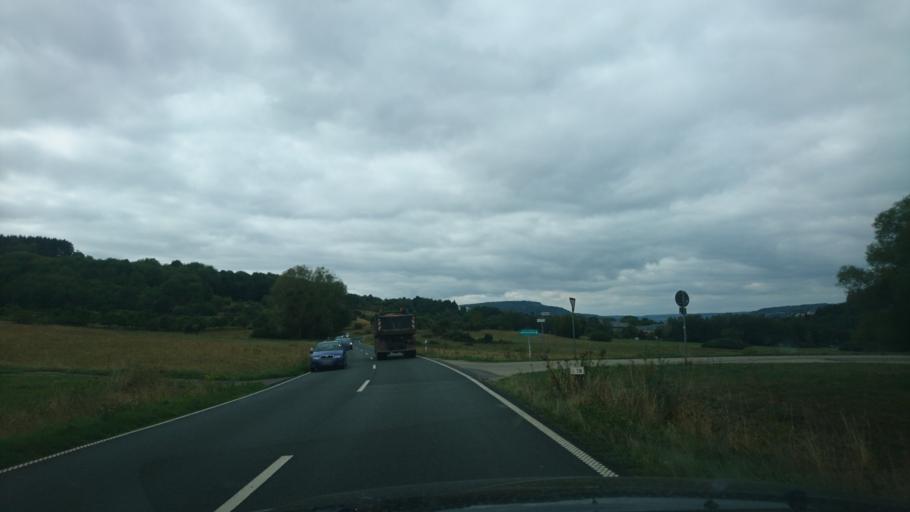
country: DE
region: Rheinland-Pfalz
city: Konz
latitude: 49.6902
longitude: 6.5934
